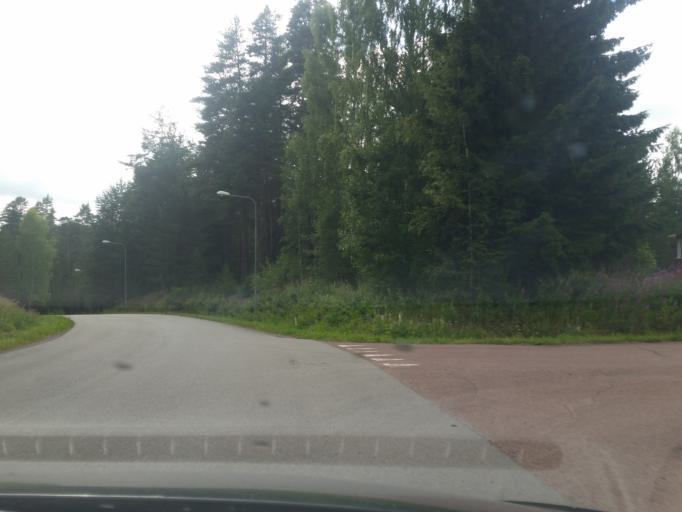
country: SE
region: Dalarna
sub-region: Leksand Municipality
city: Leksand
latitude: 60.7134
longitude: 14.9926
